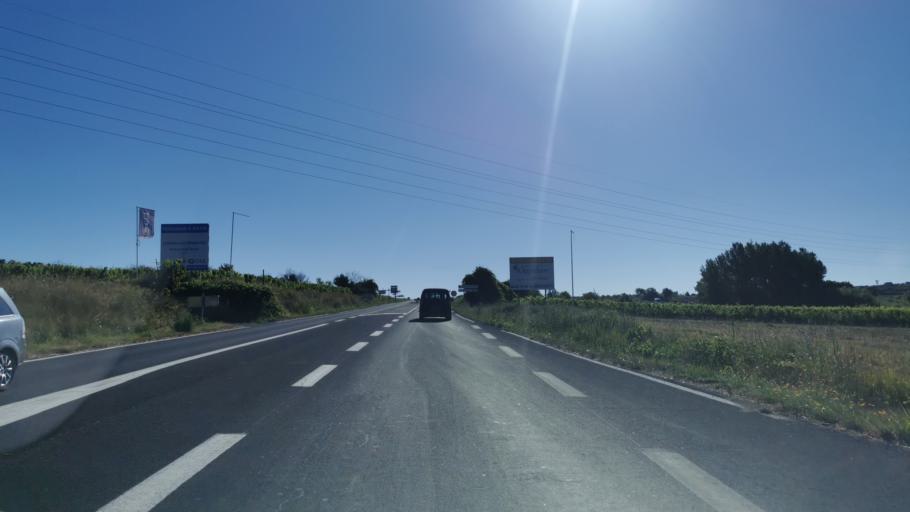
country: FR
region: Languedoc-Roussillon
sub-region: Departement de l'Herault
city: Nissan-lez-Enserune
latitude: 43.2937
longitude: 3.1283
